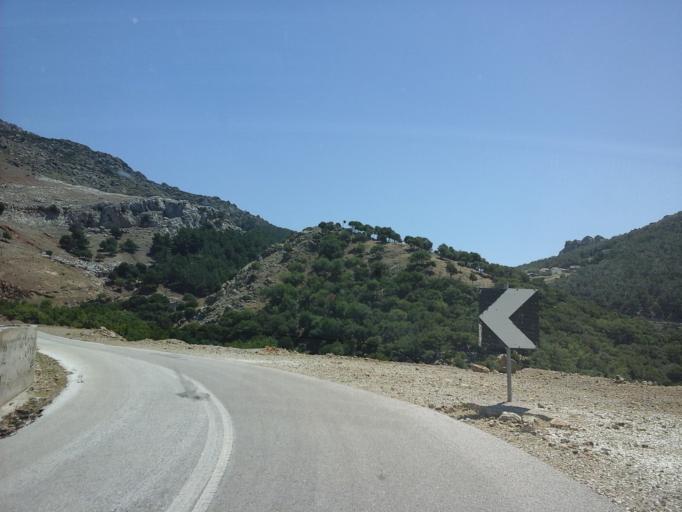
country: GR
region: East Macedonia and Thrace
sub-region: Nomos Evrou
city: Samothraki
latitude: 40.4825
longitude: 25.5232
